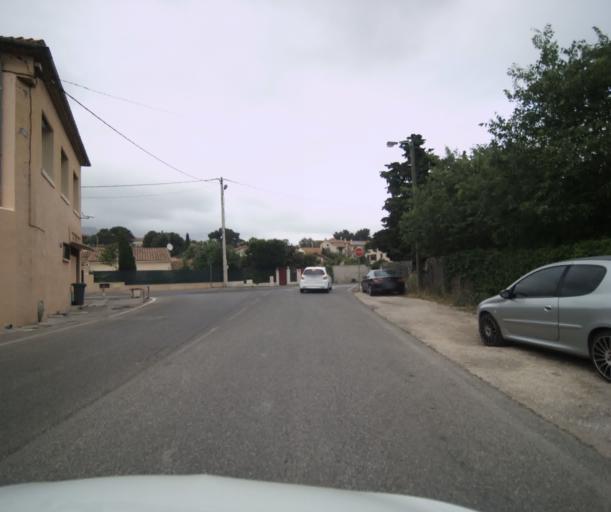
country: FR
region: Provence-Alpes-Cote d'Azur
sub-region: Departement du Var
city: La Seyne-sur-Mer
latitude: 43.1269
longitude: 5.8888
